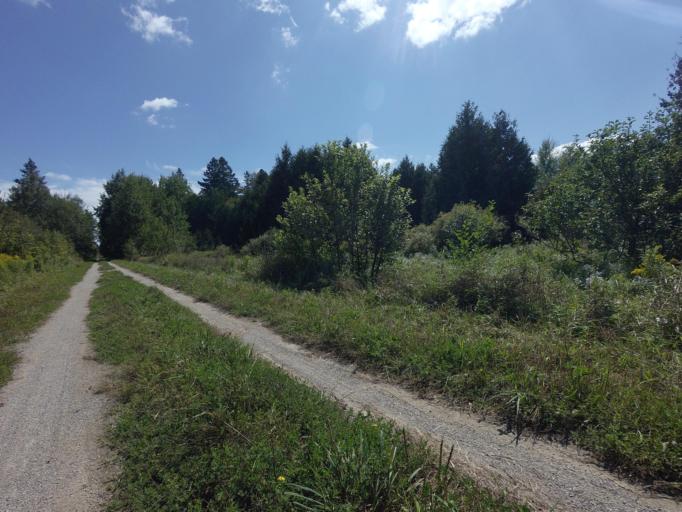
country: CA
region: Ontario
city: Orangeville
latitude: 43.7781
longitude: -80.2080
